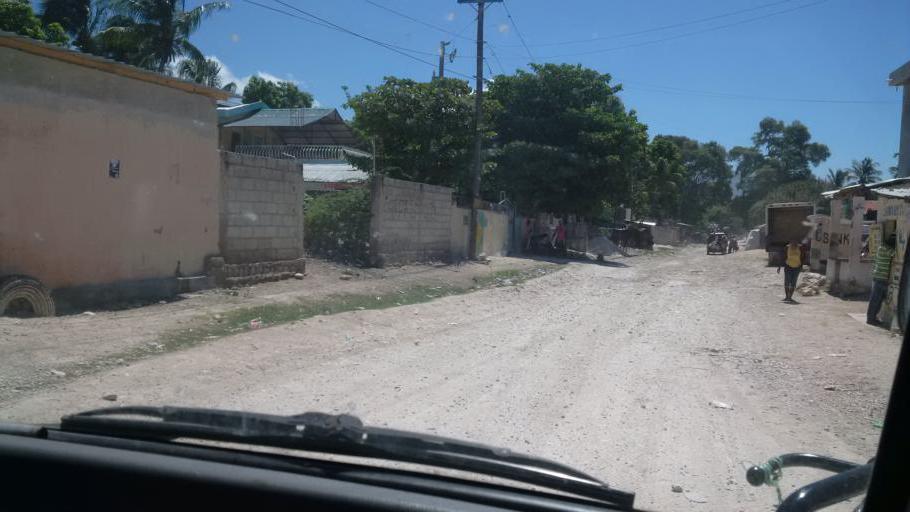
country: HT
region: Ouest
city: Thomazeau
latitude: 18.6583
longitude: -72.1493
